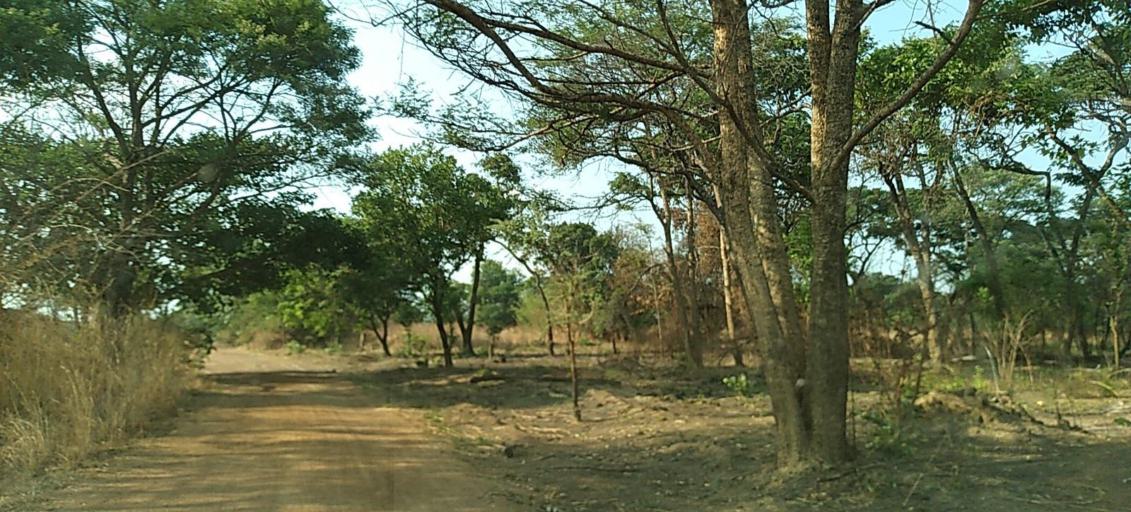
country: ZM
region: Copperbelt
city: Mpongwe
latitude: -13.4569
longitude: 28.0680
